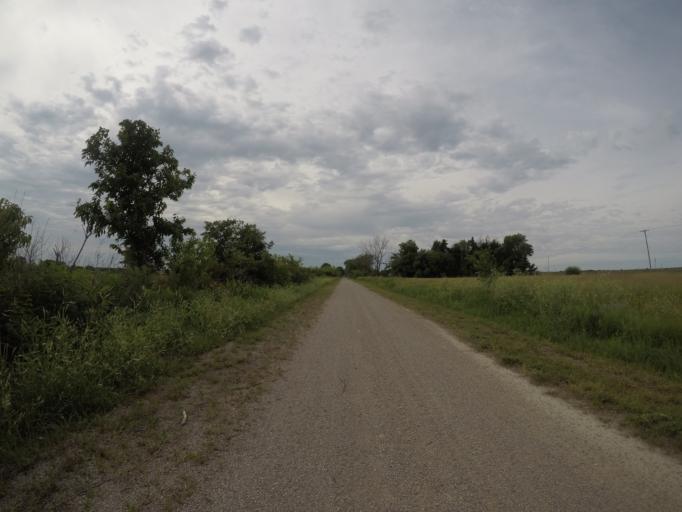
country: US
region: Kansas
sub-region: Franklin County
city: Ottawa
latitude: 38.4498
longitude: -95.2667
